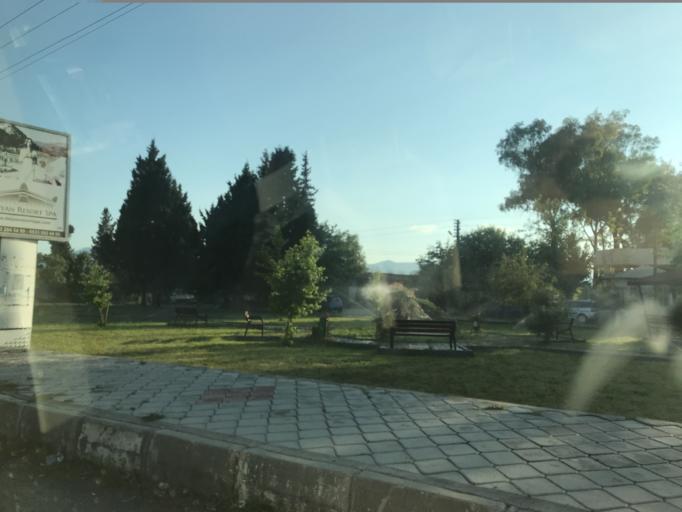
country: TR
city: Dalyan
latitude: 36.9738
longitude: 28.6864
